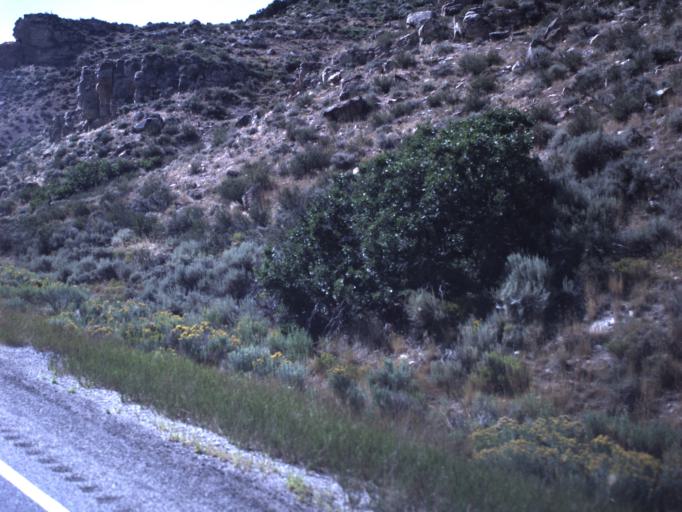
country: US
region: Utah
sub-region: Carbon County
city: Helper
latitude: 40.1928
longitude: -110.9510
